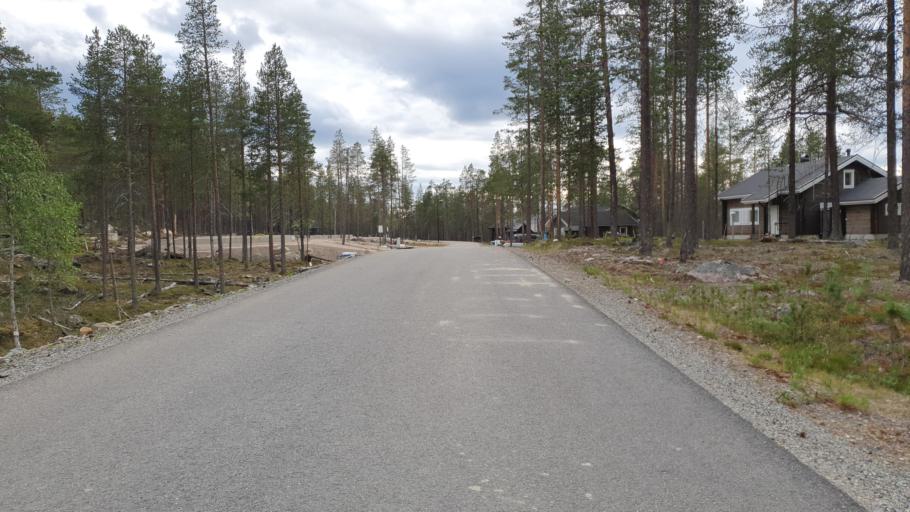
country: FI
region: Lapland
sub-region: Tunturi-Lappi
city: Kolari
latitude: 67.5891
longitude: 24.1213
